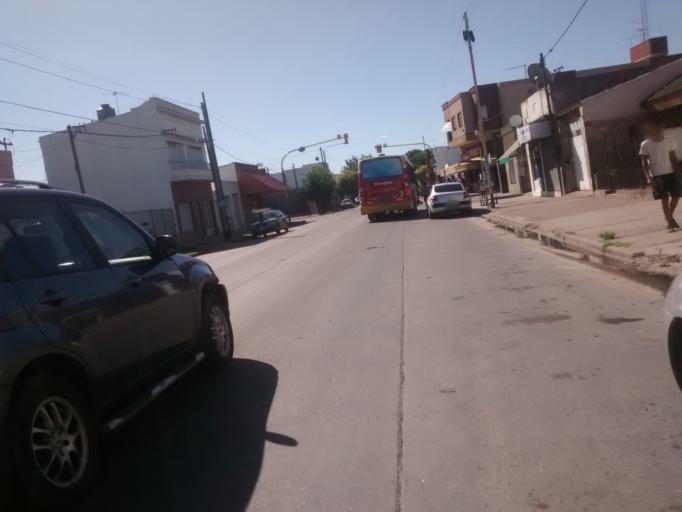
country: AR
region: Buenos Aires
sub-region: Partido de La Plata
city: La Plata
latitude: -34.9217
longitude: -57.9076
